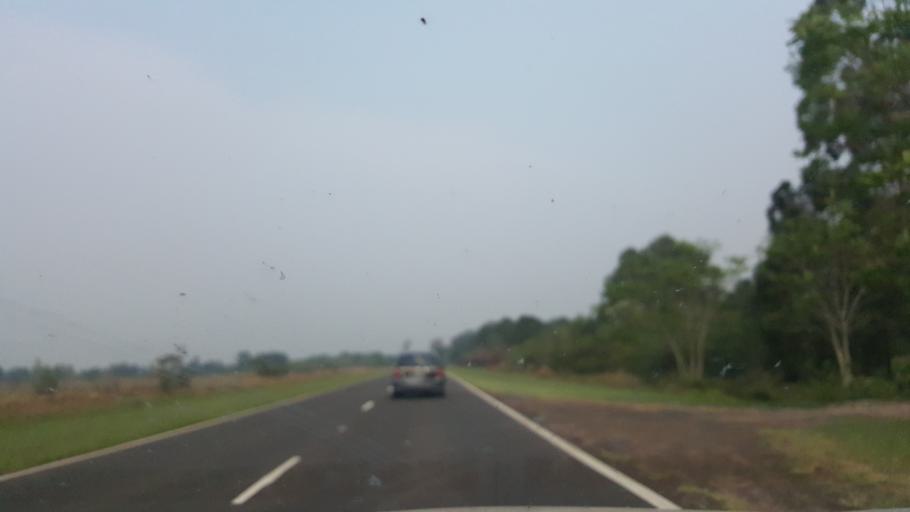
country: AR
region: Corrientes
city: Ita Ibate
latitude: -27.5084
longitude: -57.2409
